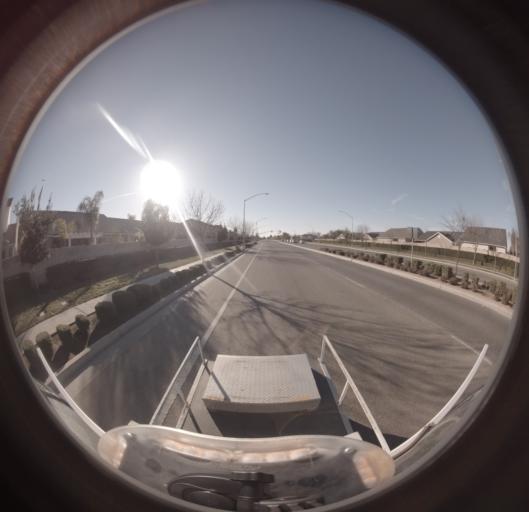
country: US
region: California
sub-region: Monterey County
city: King City
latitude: 36.1166
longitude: -120.9011
